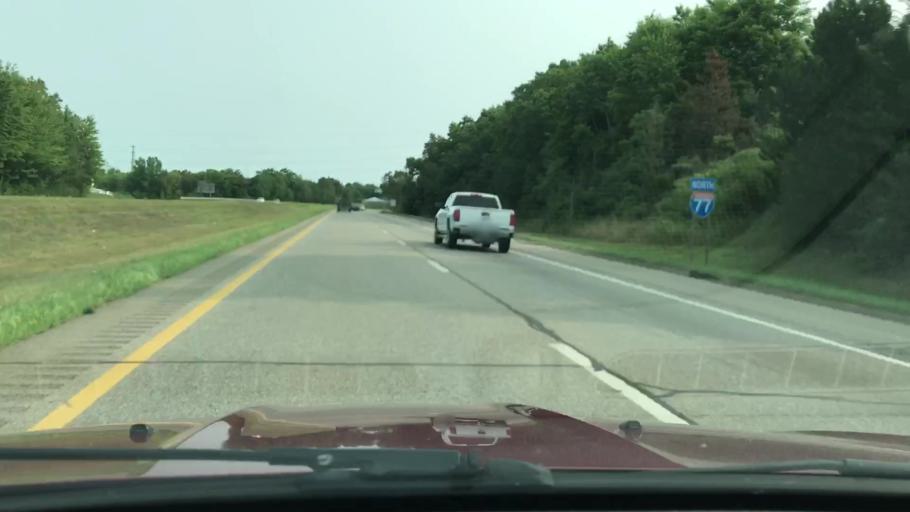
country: US
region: Ohio
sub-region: Stark County
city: Canton
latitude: 40.7585
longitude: -81.4034
